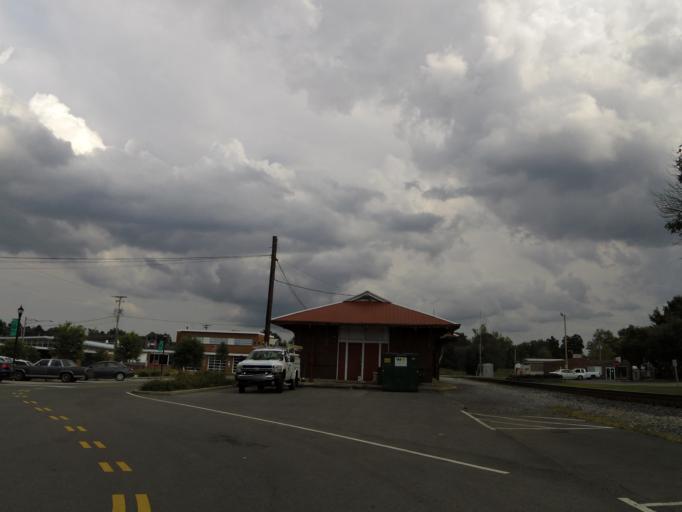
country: US
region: Tennessee
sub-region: Dickson County
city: Dickson
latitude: 36.0756
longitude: -87.3888
